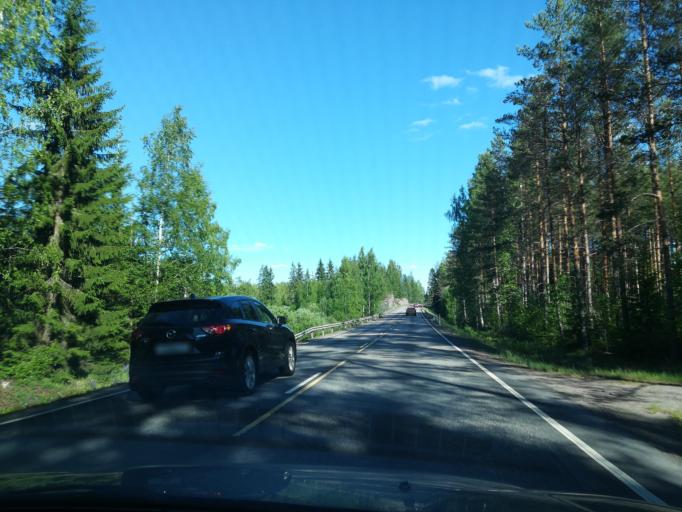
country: FI
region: South Karelia
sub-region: Imatra
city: Ruokolahti
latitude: 61.3642
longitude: 28.6930
